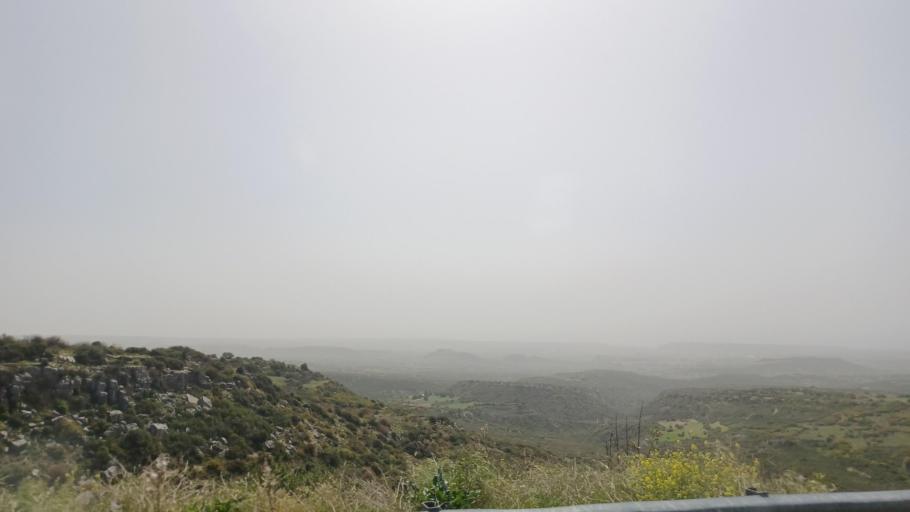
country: CY
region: Limassol
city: Pissouri
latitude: 34.7241
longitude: 32.7289
